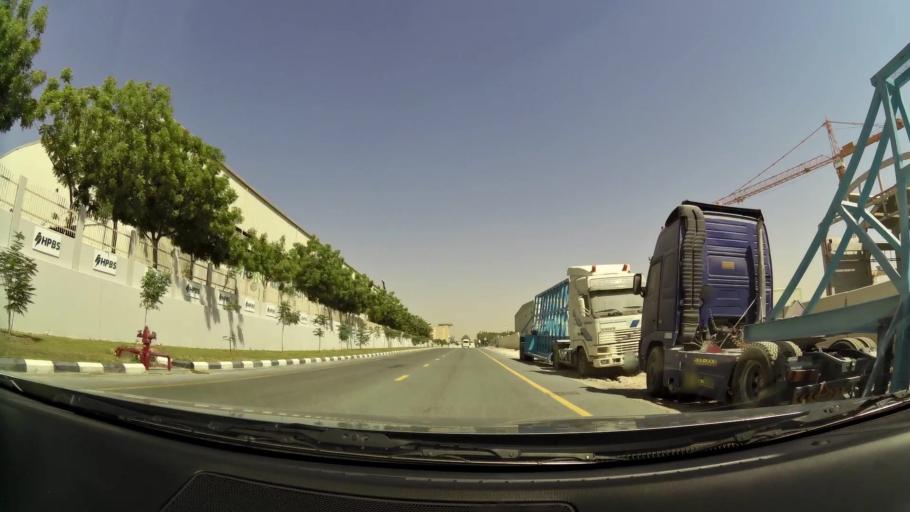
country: AE
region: Dubai
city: Dubai
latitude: 24.9720
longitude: 55.1778
